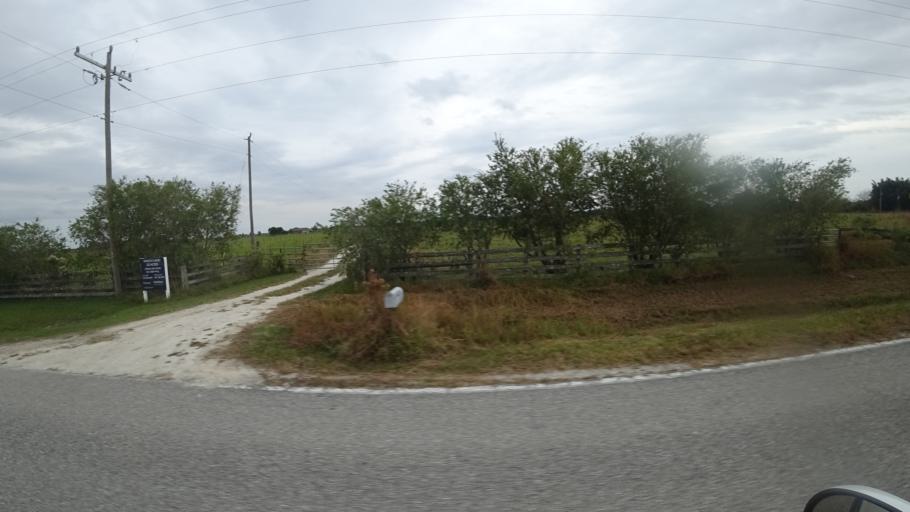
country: US
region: Florida
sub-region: Sarasota County
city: Warm Mineral Springs
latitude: 27.2829
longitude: -82.1939
